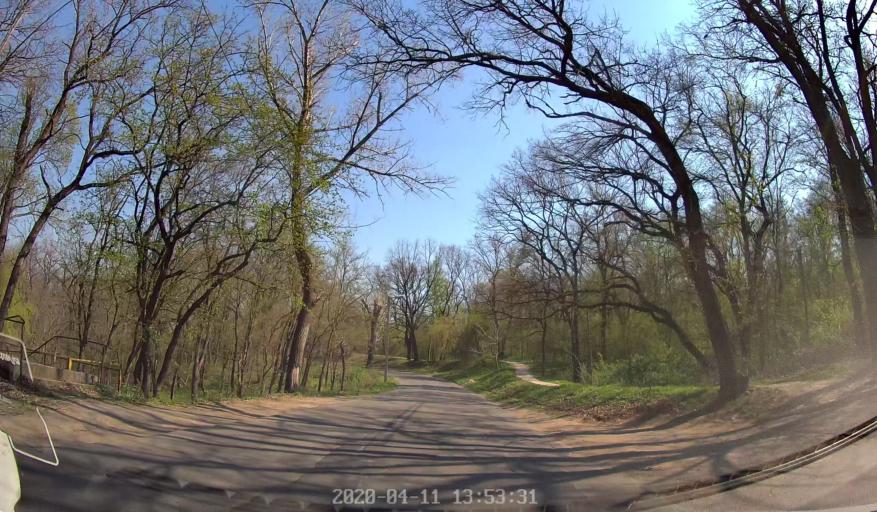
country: MD
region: Chisinau
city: Vadul lui Voda
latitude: 47.0781
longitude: 29.0952
